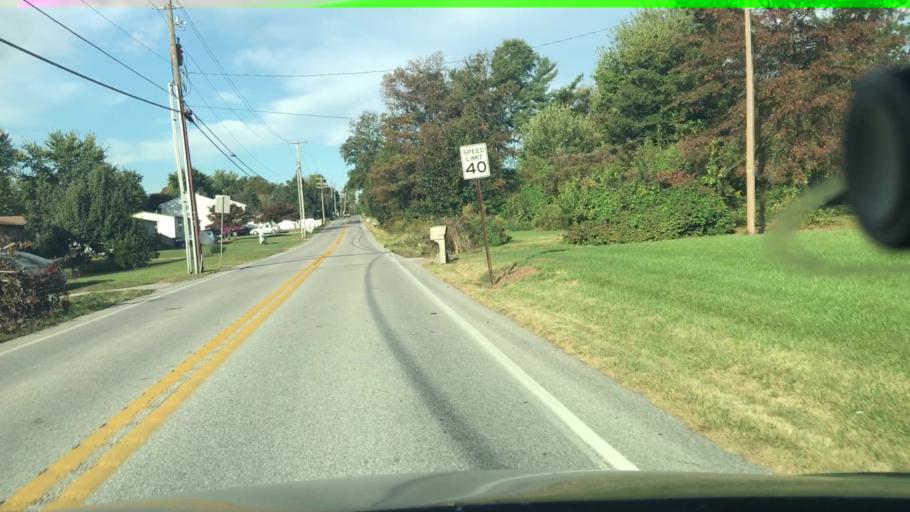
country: US
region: Pennsylvania
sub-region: York County
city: Weigelstown
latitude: 40.0182
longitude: -76.8050
